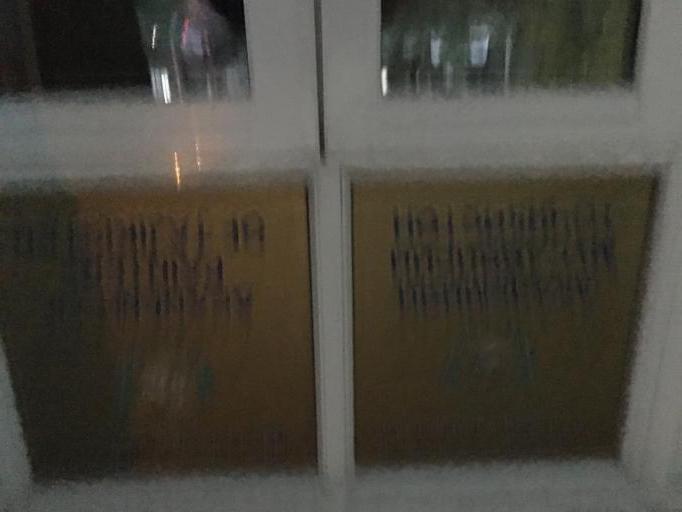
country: TJ
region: Dushanbe
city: Dushanbe
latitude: 38.5774
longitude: 68.7536
